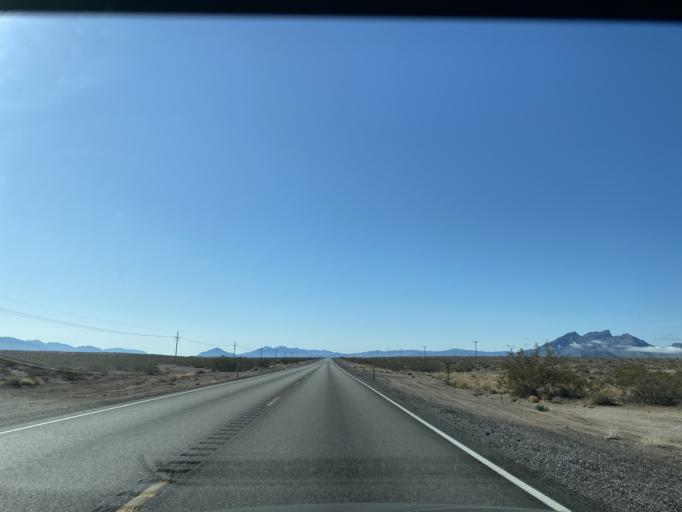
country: US
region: Nevada
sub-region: Nye County
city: Pahrump
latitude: 36.4741
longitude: -116.4217
